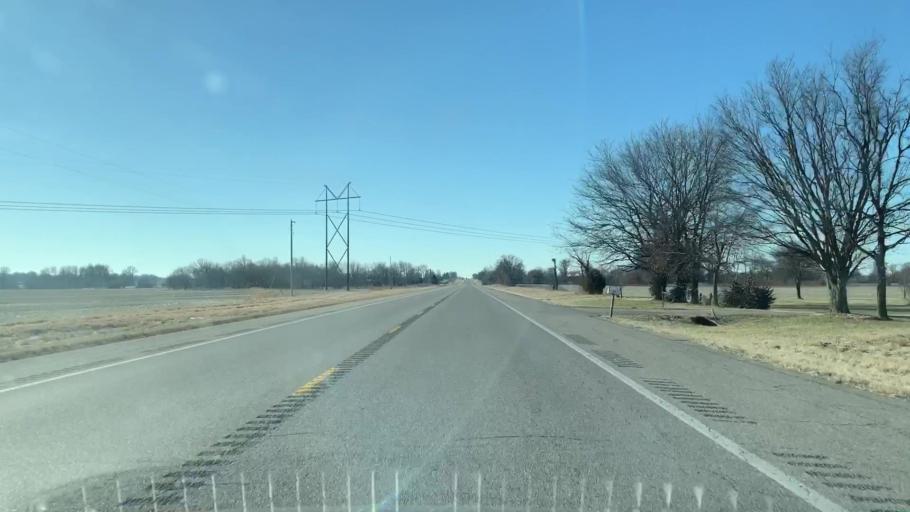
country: US
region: Kansas
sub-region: Crawford County
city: Pittsburg
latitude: 37.2917
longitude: -94.7050
